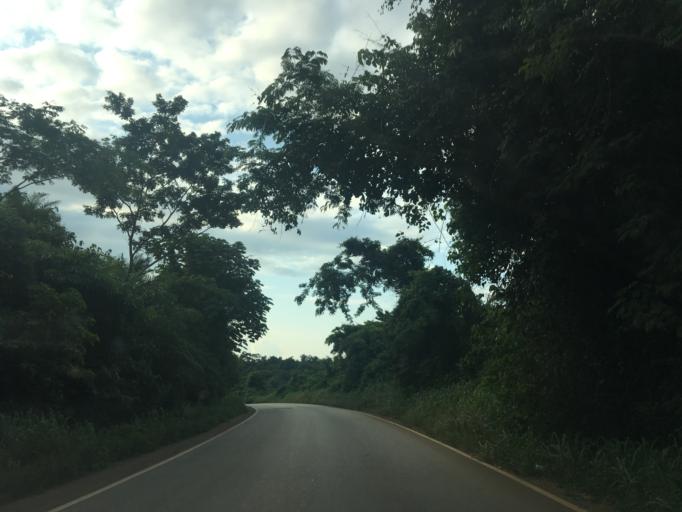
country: GH
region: Western
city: Bibiani
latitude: 6.4103
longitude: -2.3011
